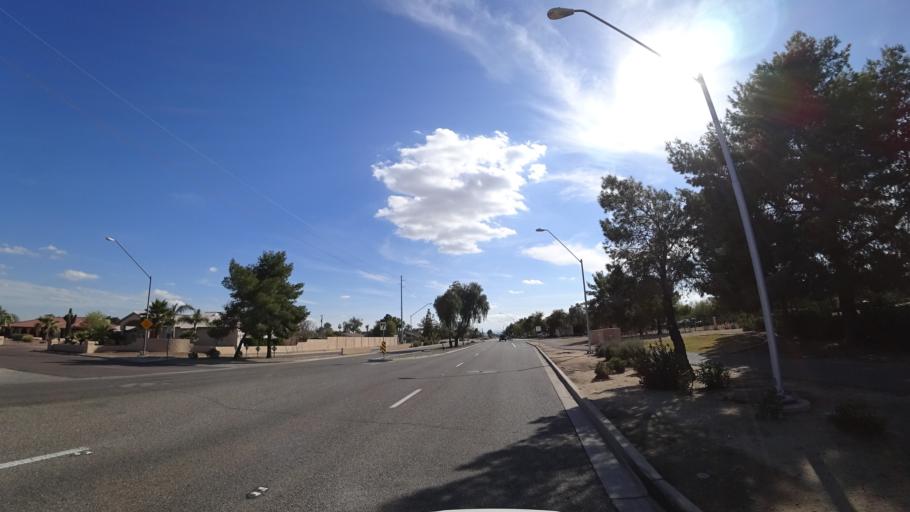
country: US
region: Arizona
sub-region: Maricopa County
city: Peoria
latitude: 33.6456
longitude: -112.2204
